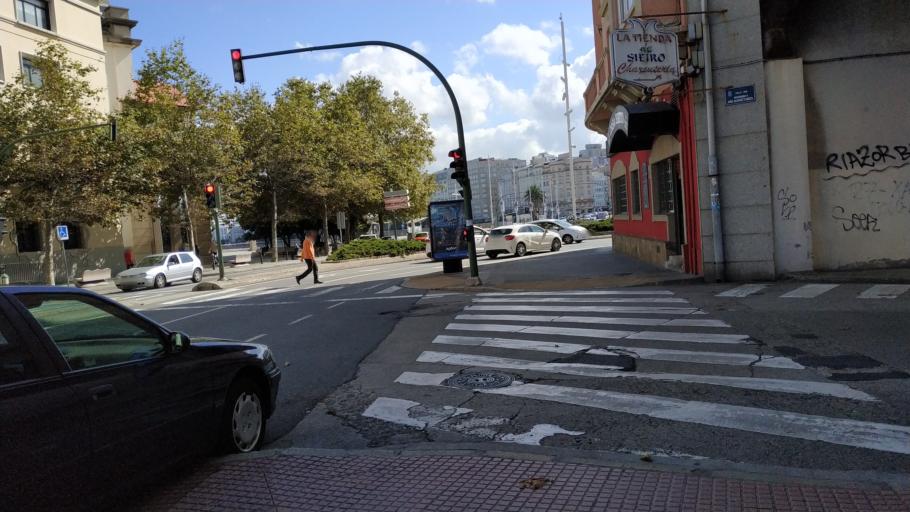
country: ES
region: Galicia
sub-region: Provincia da Coruna
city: A Coruna
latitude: 43.3701
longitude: -8.4161
